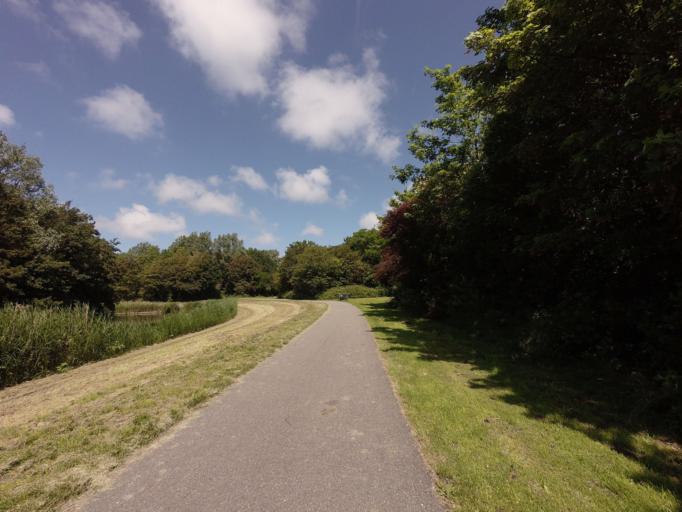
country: NL
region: North Holland
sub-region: Gemeente Den Helder
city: Den Helder
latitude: 52.9330
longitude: 4.7654
